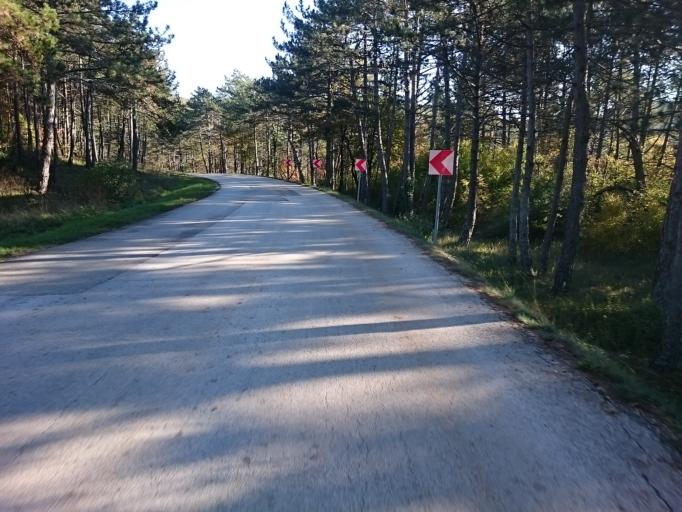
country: HR
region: Istarska
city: Buje
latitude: 45.3922
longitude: 13.7163
